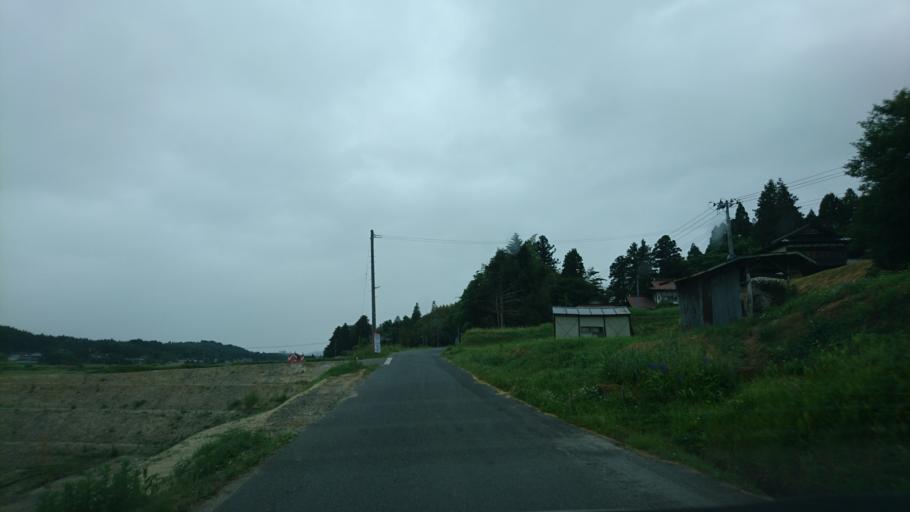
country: JP
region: Iwate
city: Ichinoseki
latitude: 38.9148
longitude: 141.1790
